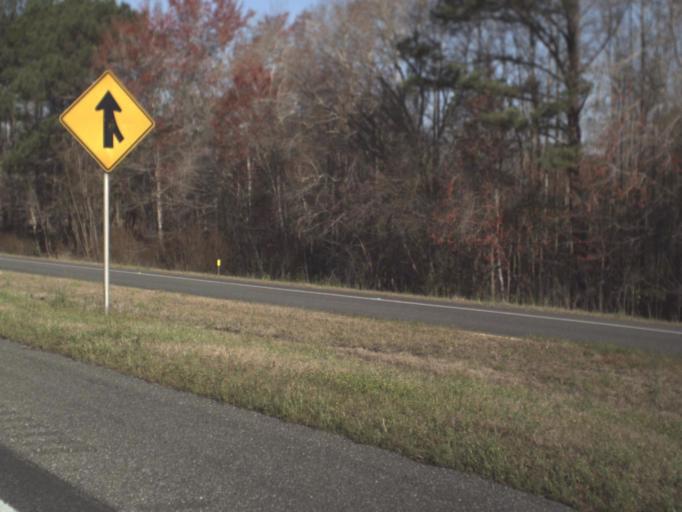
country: US
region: Florida
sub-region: Jefferson County
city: Monticello
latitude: 30.4567
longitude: -83.7662
